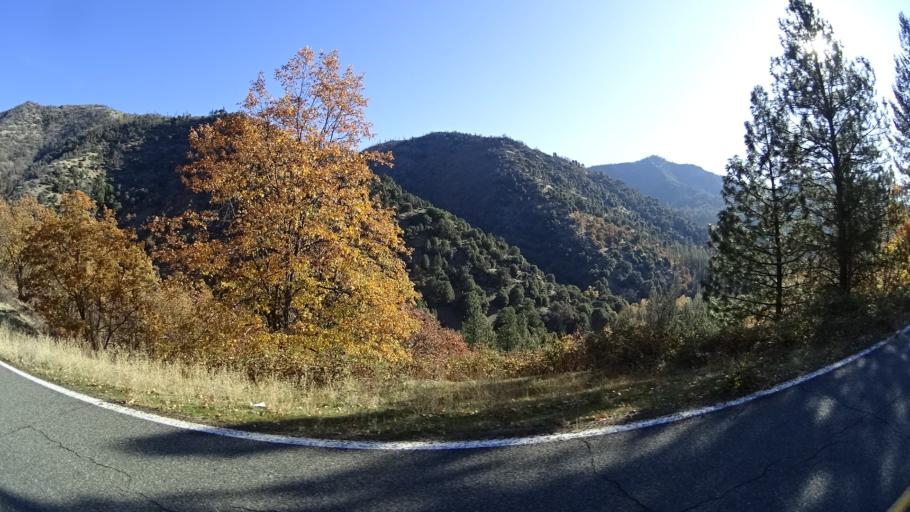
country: US
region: California
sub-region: Siskiyou County
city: Yreka
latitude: 41.9032
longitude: -122.8306
